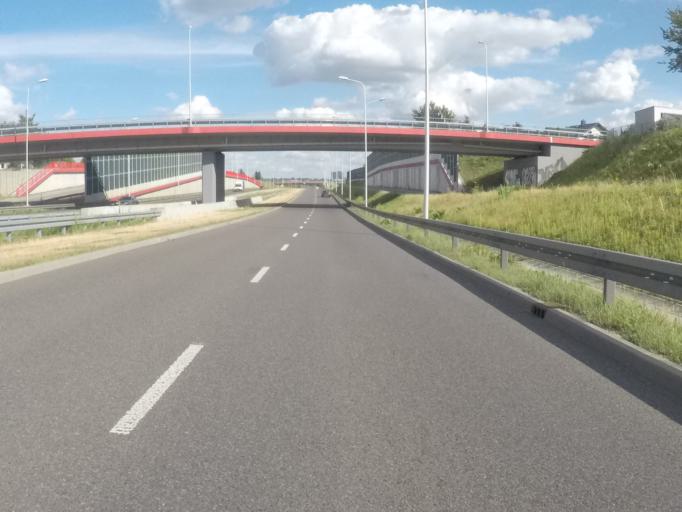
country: PL
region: Lublin Voivodeship
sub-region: Powiat lubelski
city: Jastkow
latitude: 51.2676
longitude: 22.4877
